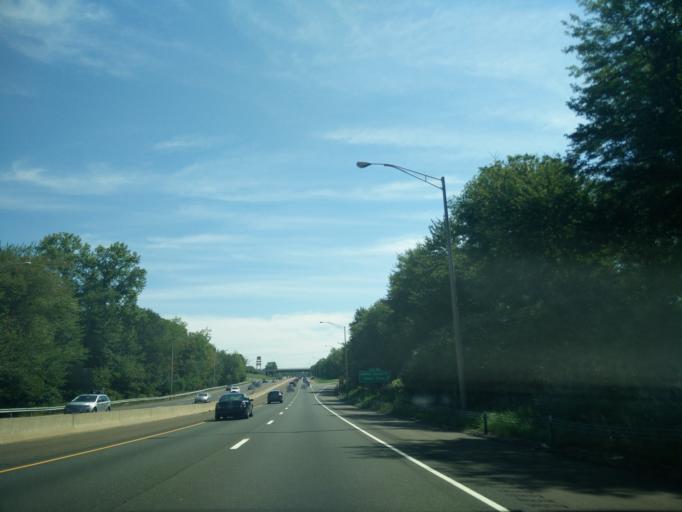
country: US
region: Connecticut
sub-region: New Haven County
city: North Branford
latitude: 41.2945
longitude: -72.7706
